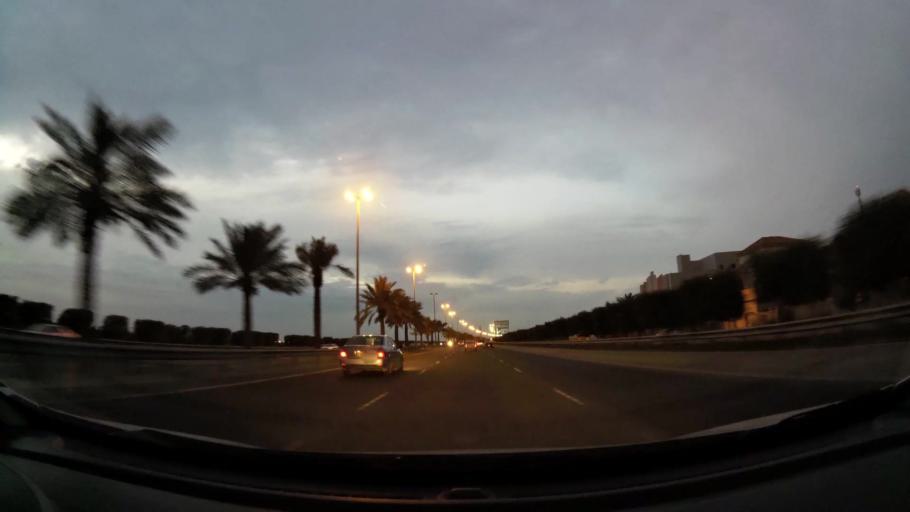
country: BH
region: Central Governorate
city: Madinat Hamad
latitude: 26.1562
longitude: 50.5063
